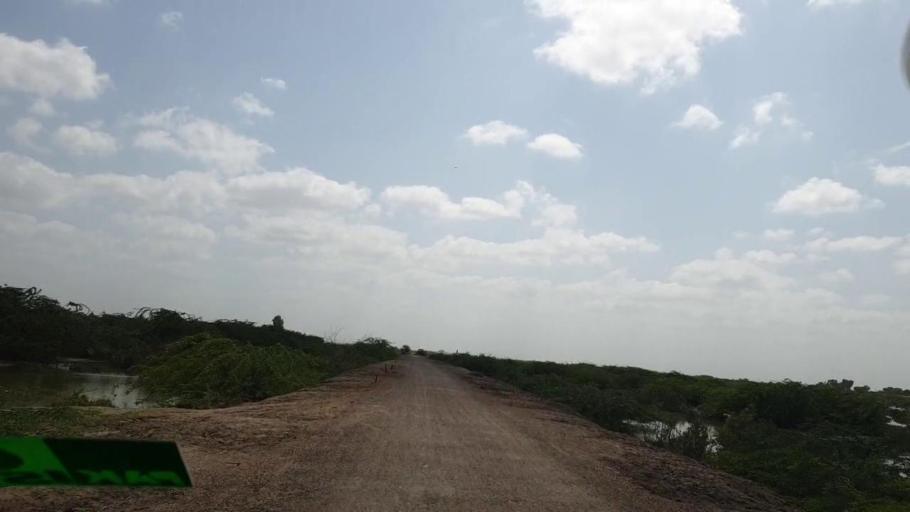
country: PK
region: Sindh
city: Kadhan
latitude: 24.5923
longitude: 69.1831
